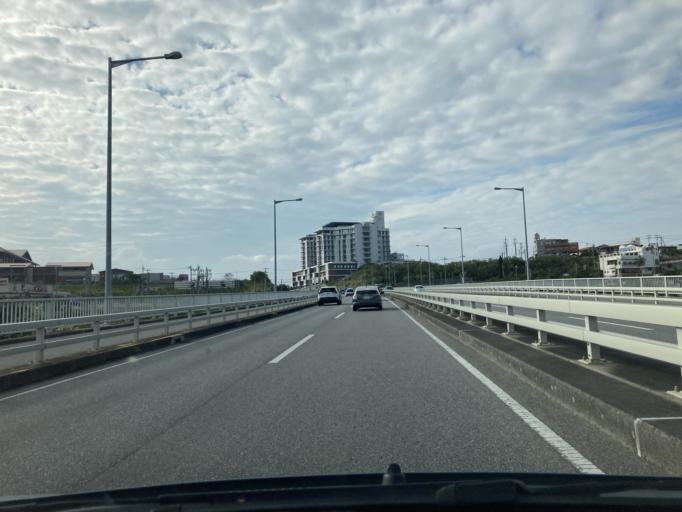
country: JP
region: Okinawa
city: Okinawa
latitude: 26.3156
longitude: 127.8016
